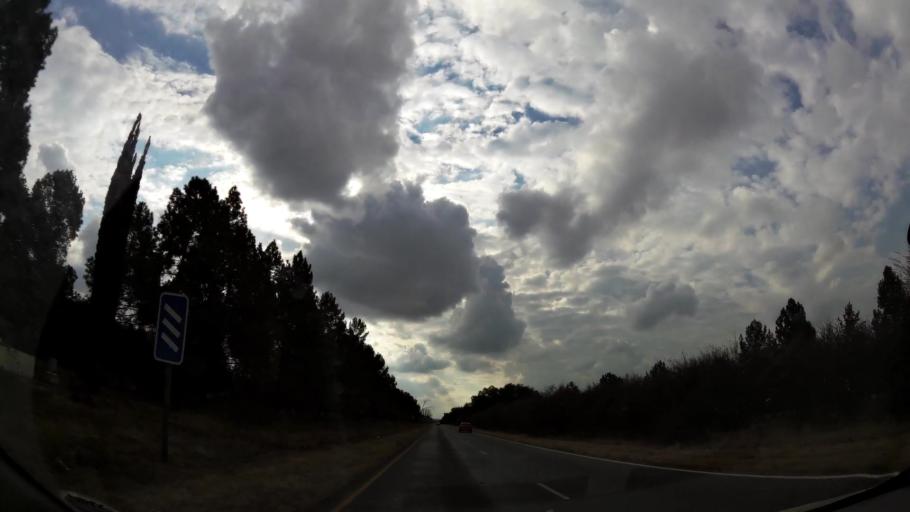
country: ZA
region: Orange Free State
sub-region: Fezile Dabi District Municipality
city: Sasolburg
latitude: -26.8066
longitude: 27.8362
